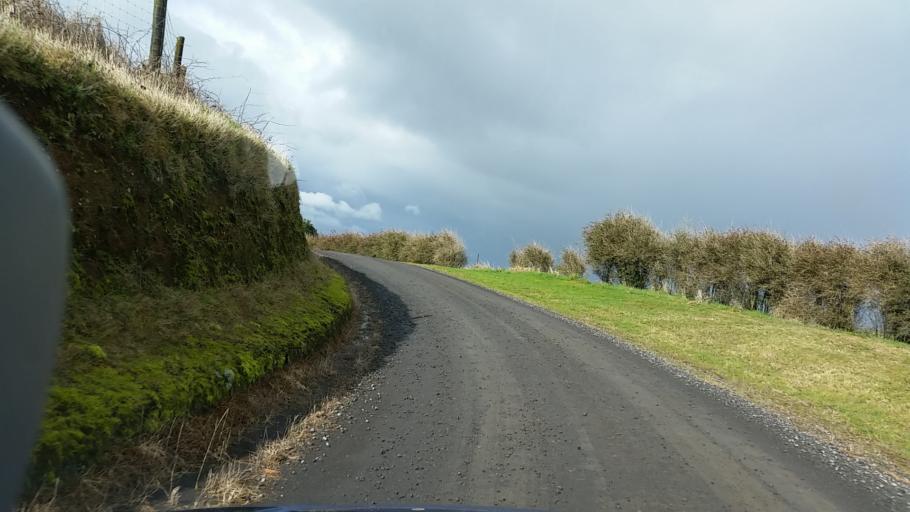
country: NZ
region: Taranaki
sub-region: South Taranaki District
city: Eltham
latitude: -39.2829
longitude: 174.3085
